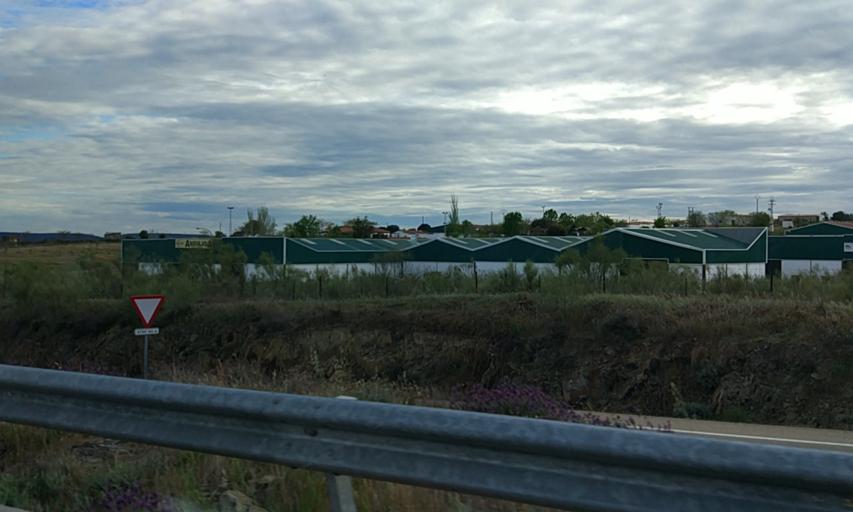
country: ES
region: Extremadura
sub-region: Provincia de Caceres
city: Torrejoncillo
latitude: 39.9059
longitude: -6.4772
